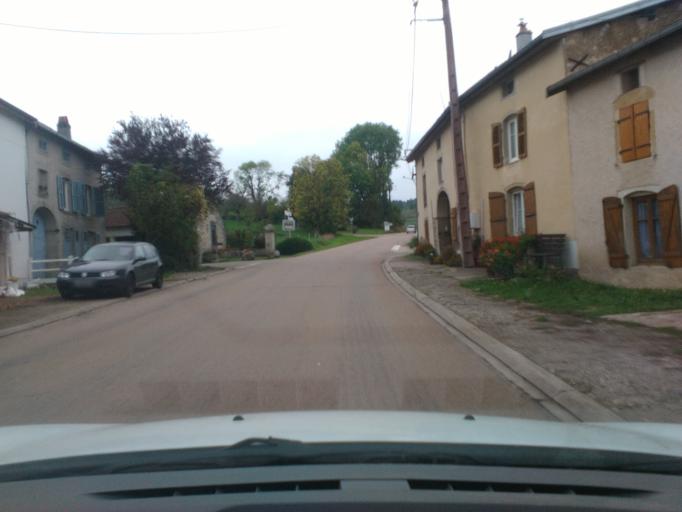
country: FR
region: Lorraine
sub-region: Departement des Vosges
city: Vincey
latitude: 48.3009
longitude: 6.2700
